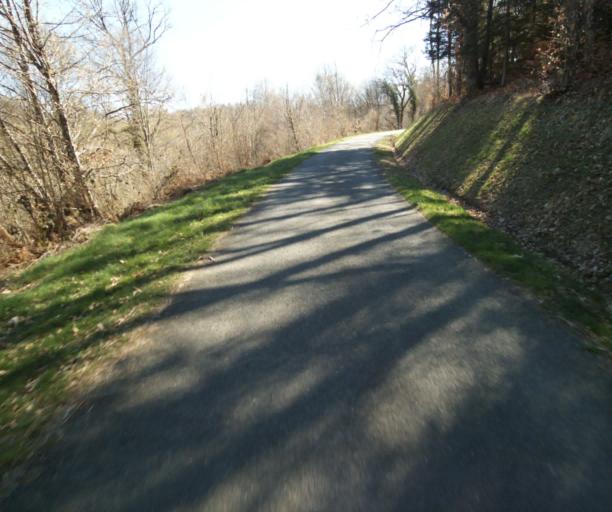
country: FR
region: Limousin
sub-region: Departement de la Correze
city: Chamboulive
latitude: 45.4145
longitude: 1.6508
